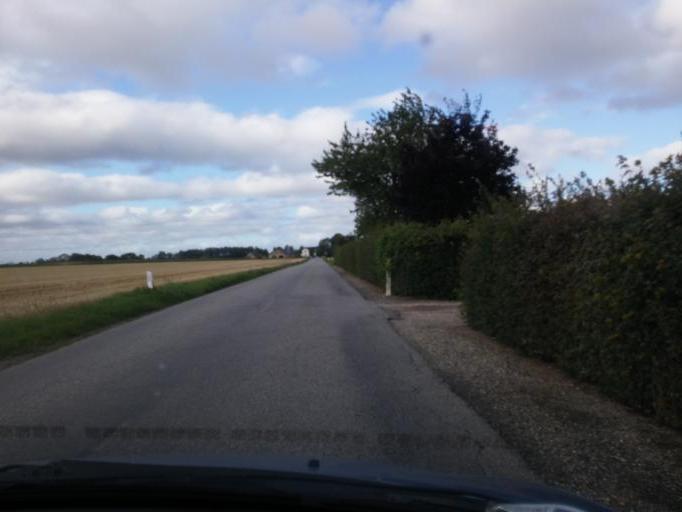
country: DK
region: South Denmark
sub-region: Odense Kommune
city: Bullerup
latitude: 55.3986
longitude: 10.5094
